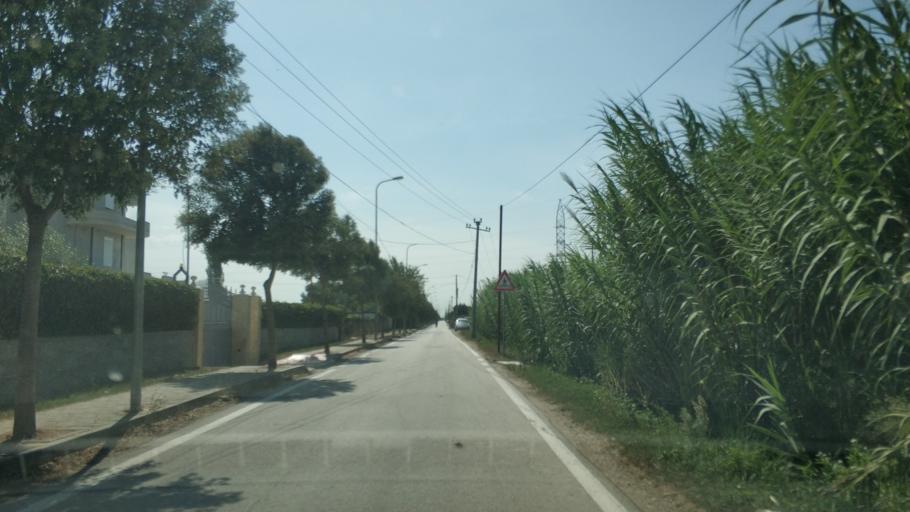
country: AL
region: Fier
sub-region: Rrethi i Fierit
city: Dermenas
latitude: 40.7367
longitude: 19.4758
